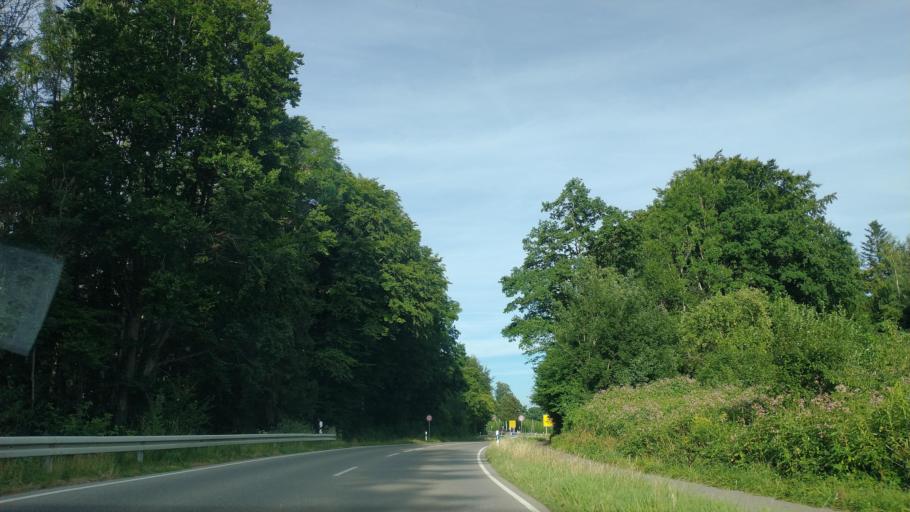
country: DE
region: Baden-Wuerttemberg
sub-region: Tuebingen Region
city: Neukirch
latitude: 47.6564
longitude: 9.6693
